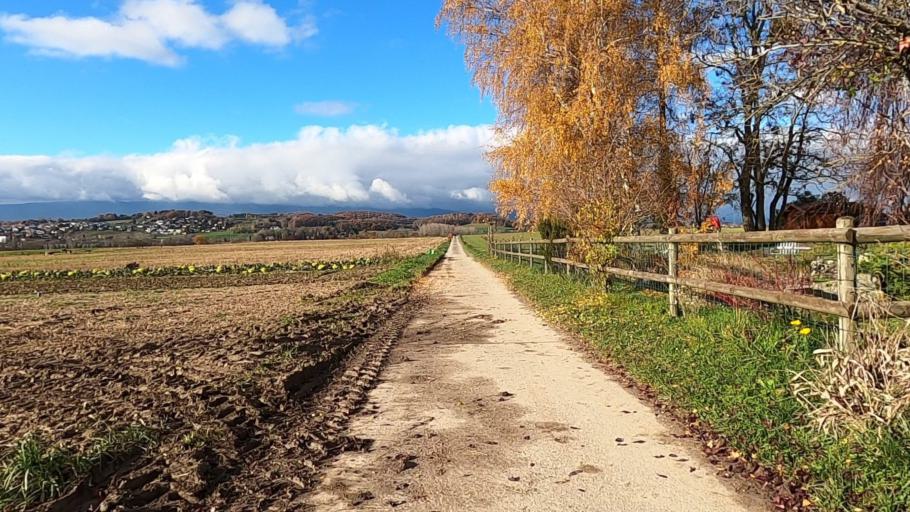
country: CH
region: Vaud
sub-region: Morges District
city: Saint-Prex
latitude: 46.5157
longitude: 6.4473
